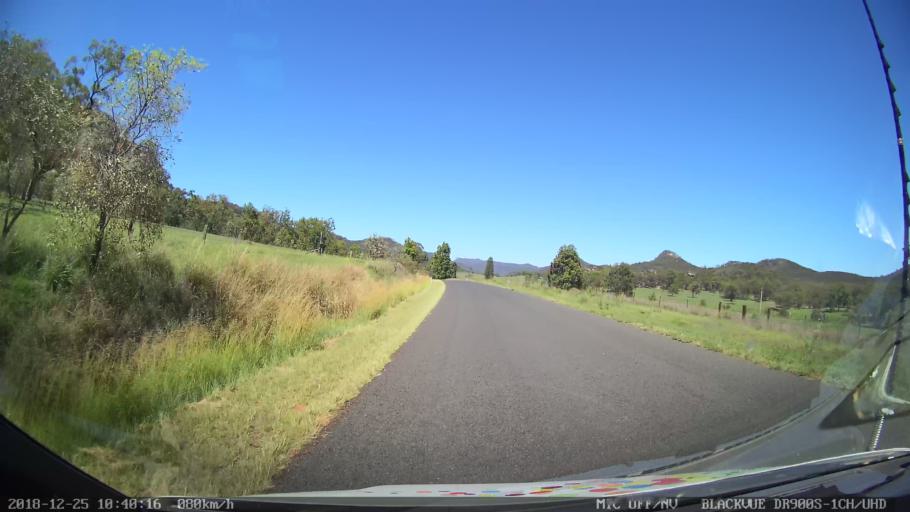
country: AU
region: New South Wales
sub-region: Upper Hunter Shire
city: Merriwa
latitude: -32.4064
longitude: 150.3449
